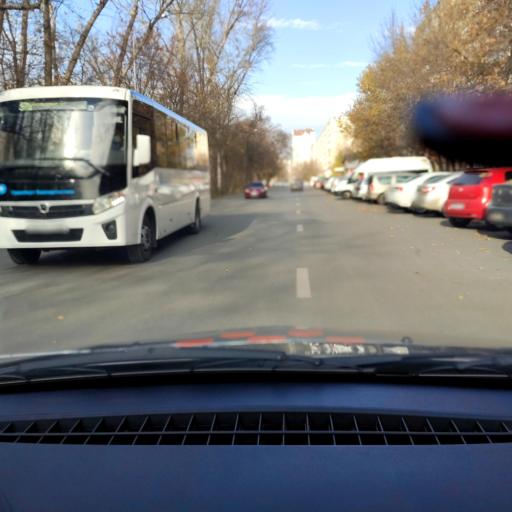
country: RU
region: Bashkortostan
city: Ufa
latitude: 54.7414
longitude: 56.0191
